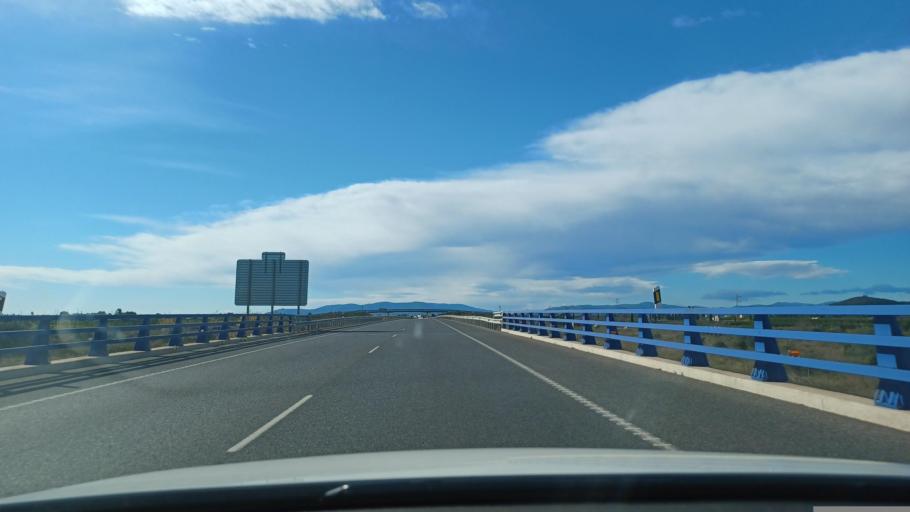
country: ES
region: Valencia
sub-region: Provincia de Castello
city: Vinaros
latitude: 40.4883
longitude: 0.4549
